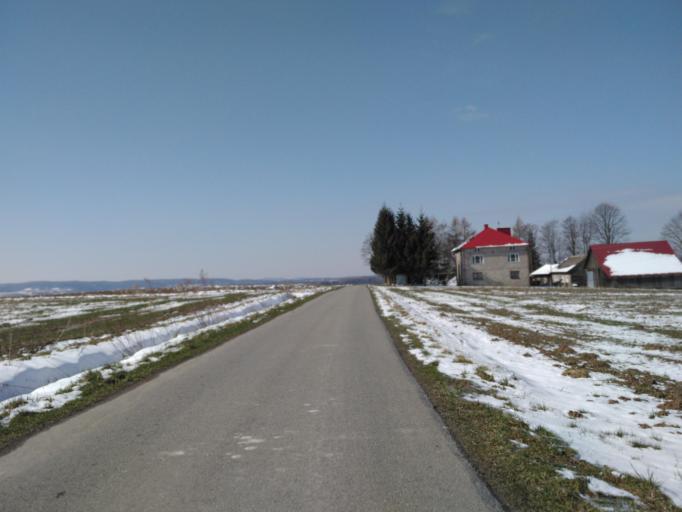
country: PL
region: Subcarpathian Voivodeship
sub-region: Powiat ropczycko-sedziszowski
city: Wielopole Skrzynskie
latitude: 49.9714
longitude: 21.6019
